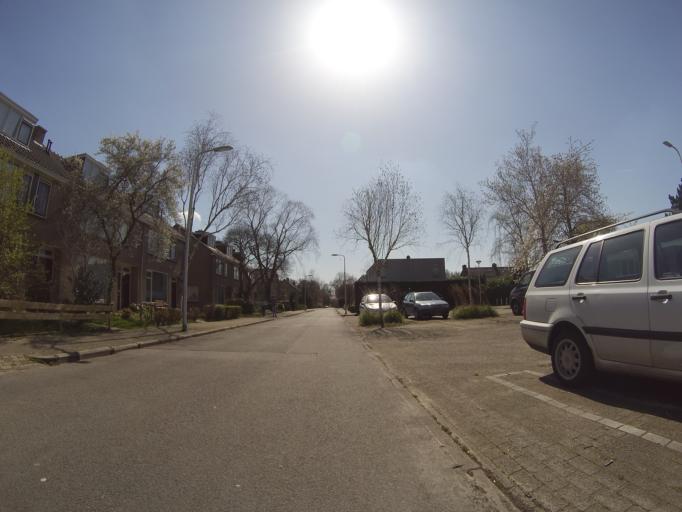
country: NL
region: Utrecht
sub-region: Gemeente Amersfoort
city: Amersfoort
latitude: 52.1689
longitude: 5.3985
